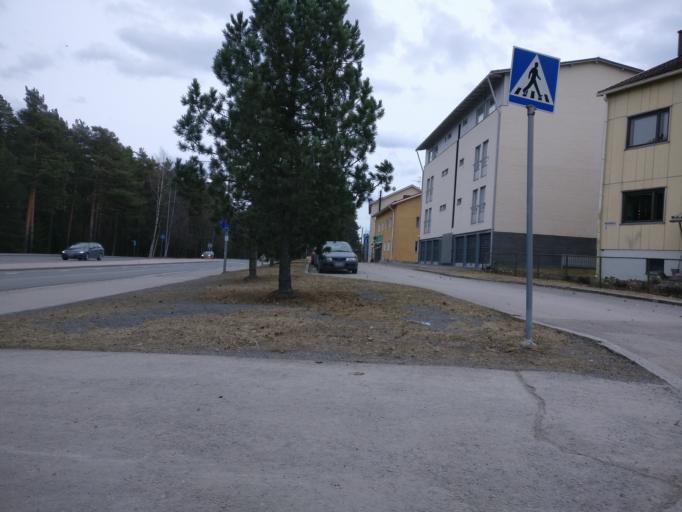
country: FI
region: Pirkanmaa
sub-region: Tampere
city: Tampere
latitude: 61.4930
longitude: 23.8046
